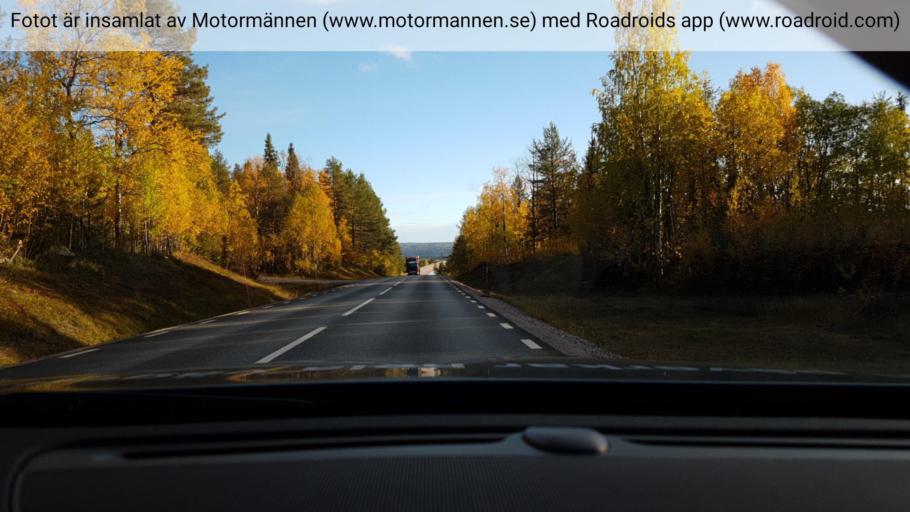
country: SE
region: Norrbotten
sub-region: Jokkmokks Kommun
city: Jokkmokk
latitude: 66.8952
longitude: 19.8274
